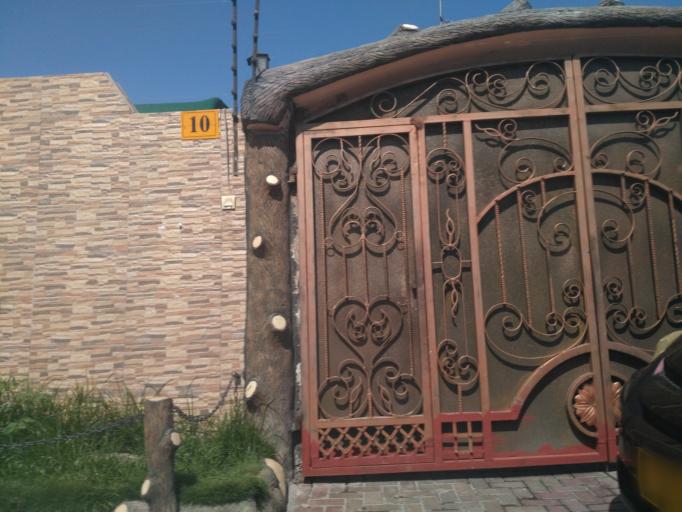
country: TZ
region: Dar es Salaam
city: Magomeni
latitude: -6.7906
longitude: 39.2656
